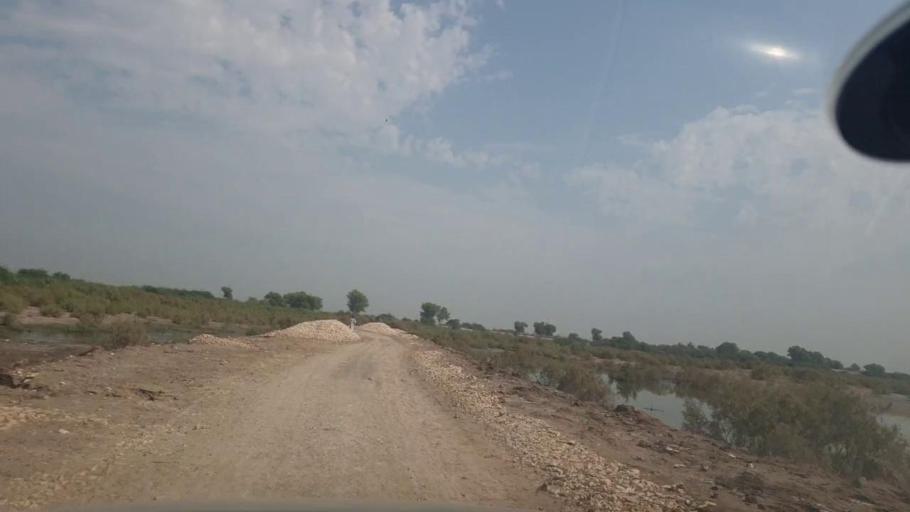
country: PK
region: Balochistan
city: Mehrabpur
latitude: 28.1148
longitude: 68.0908
